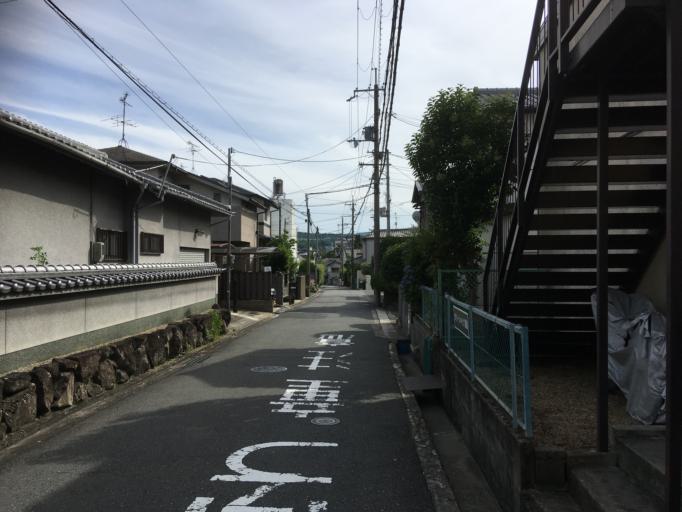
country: JP
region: Nara
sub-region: Ikoma-shi
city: Ikoma
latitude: 34.6974
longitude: 135.7382
